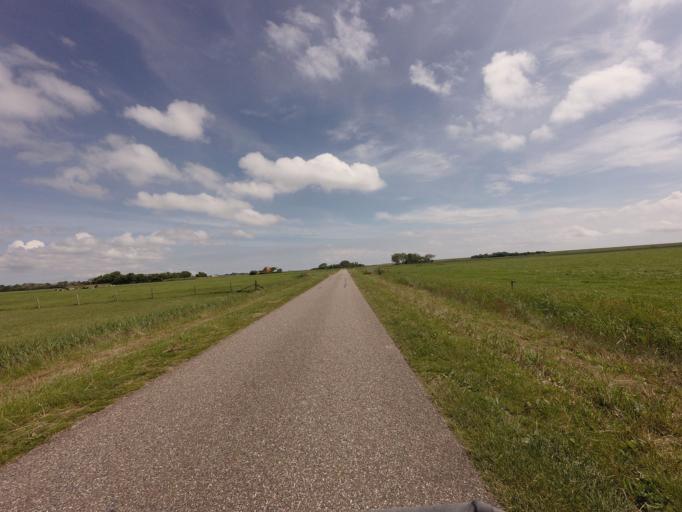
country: NL
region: North Holland
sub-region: Gemeente Texel
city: Den Burg
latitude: 53.0652
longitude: 4.8530
